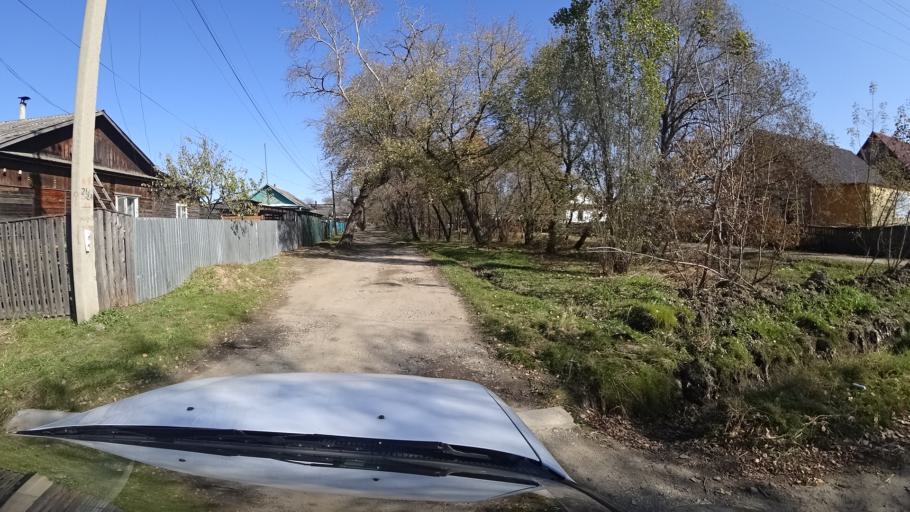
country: RU
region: Primorskiy
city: Dal'nerechensk
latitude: 45.9280
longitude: 133.7369
